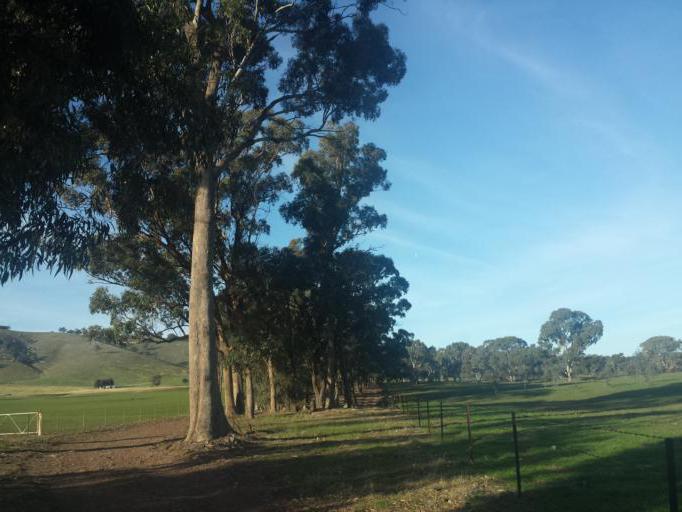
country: AU
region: Victoria
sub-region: Murrindindi
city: Kinglake West
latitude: -36.9998
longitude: 145.2256
